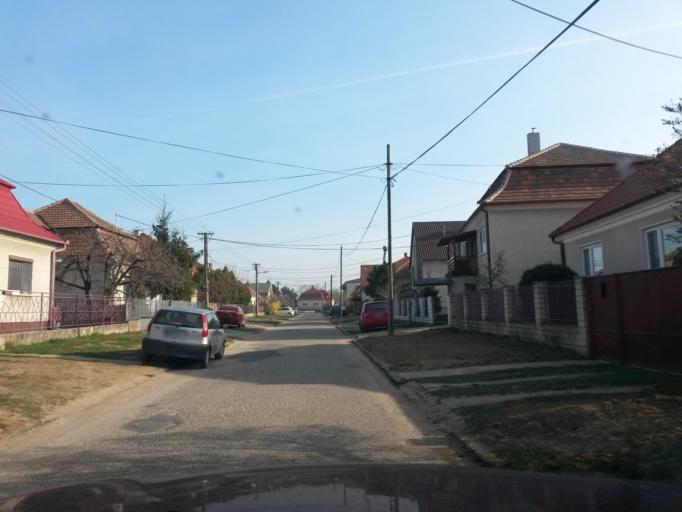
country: SK
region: Nitriansky
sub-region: Okres Komarno
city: Hurbanovo
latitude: 47.8849
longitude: 18.2052
